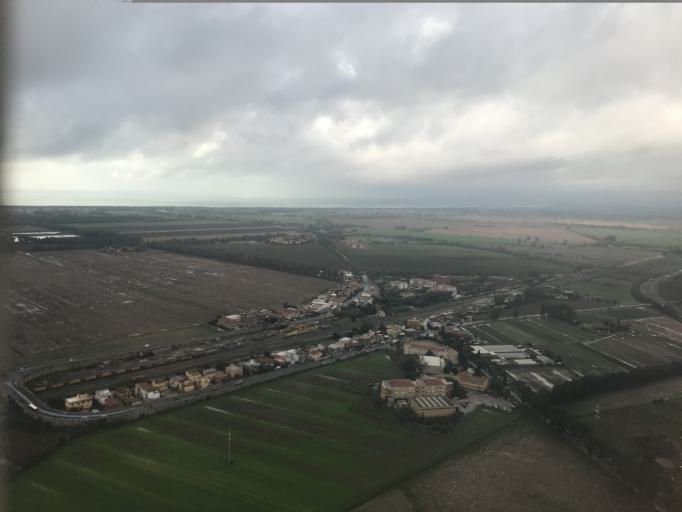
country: IT
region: Latium
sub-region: Citta metropolitana di Roma Capitale
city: Maccarese
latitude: 41.8756
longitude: 12.2495
